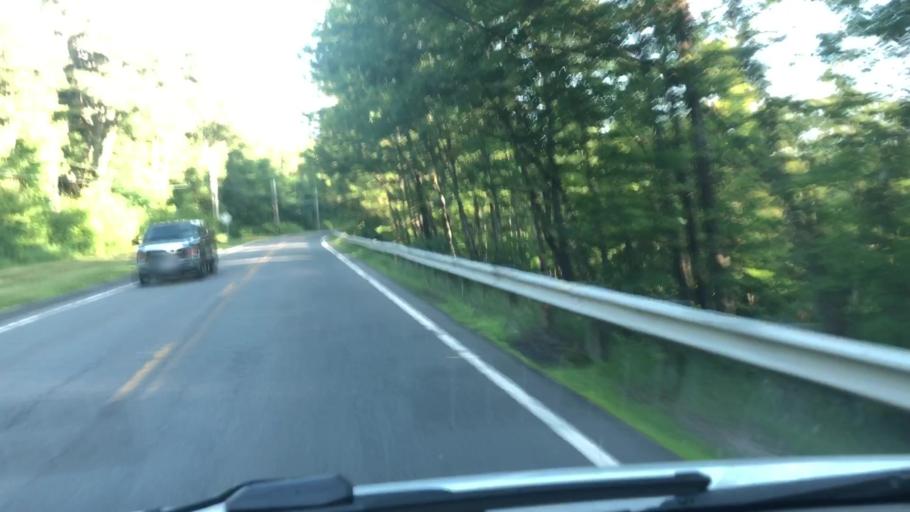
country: US
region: Massachusetts
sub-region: Hampshire County
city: Chesterfield
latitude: 42.4287
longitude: -72.7869
